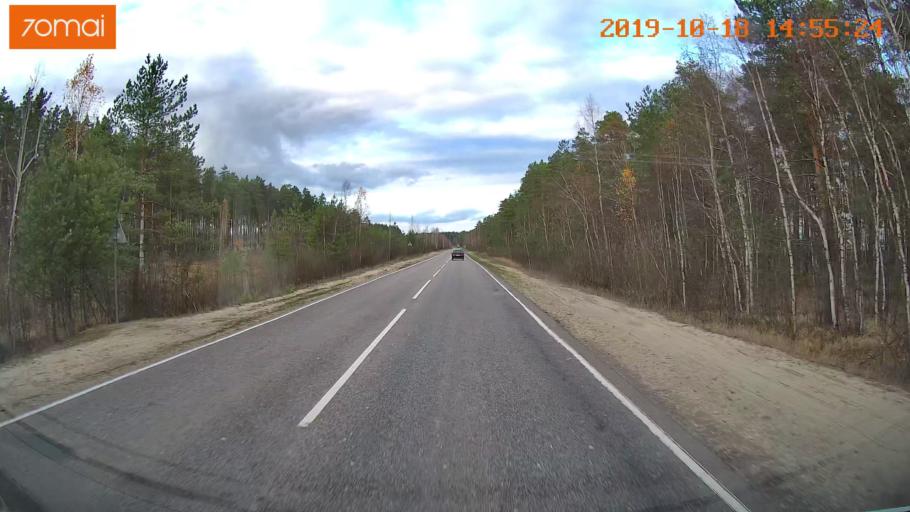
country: RU
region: Vladimir
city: Kurlovo
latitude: 55.4516
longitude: 40.5888
